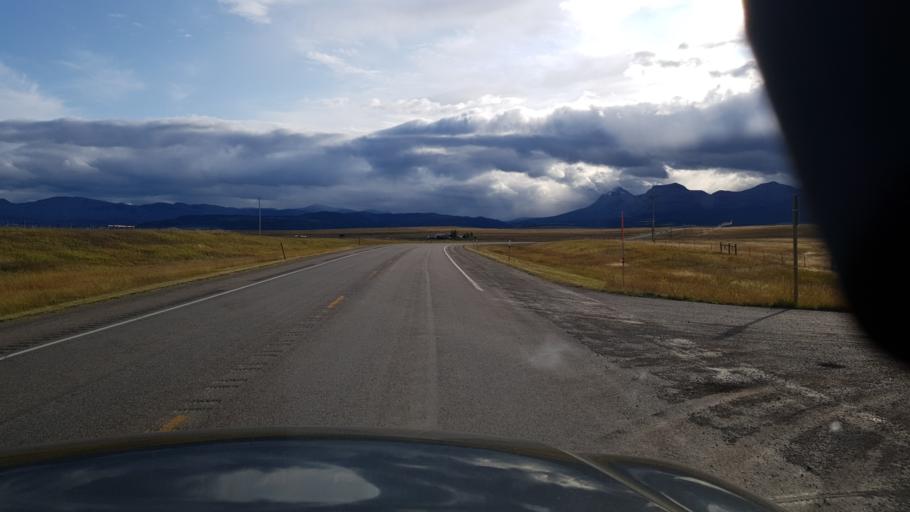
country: US
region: Montana
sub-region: Glacier County
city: South Browning
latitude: 48.4694
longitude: -113.1516
